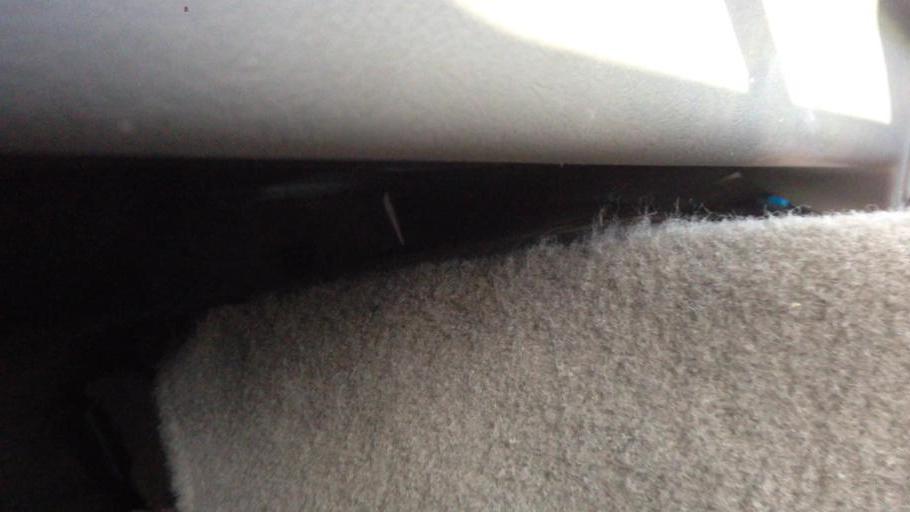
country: US
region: New York
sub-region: Columbia County
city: Lorenz Park
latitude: 42.2614
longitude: -73.7701
